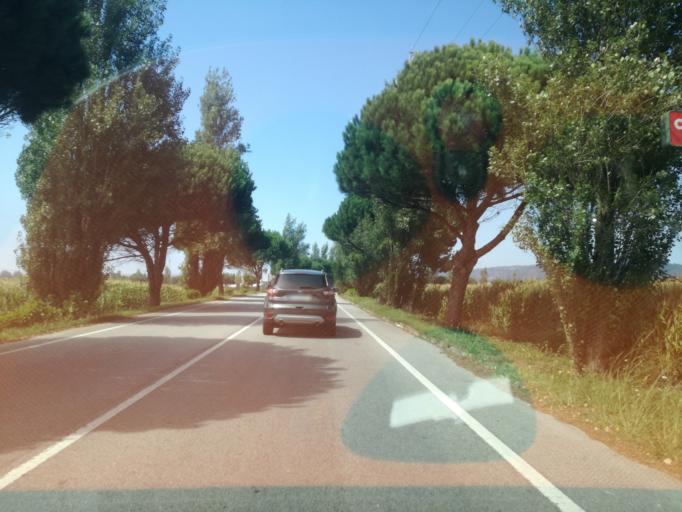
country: PT
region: Braga
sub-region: Esposende
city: Esposende
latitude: 41.5219
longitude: -8.7717
